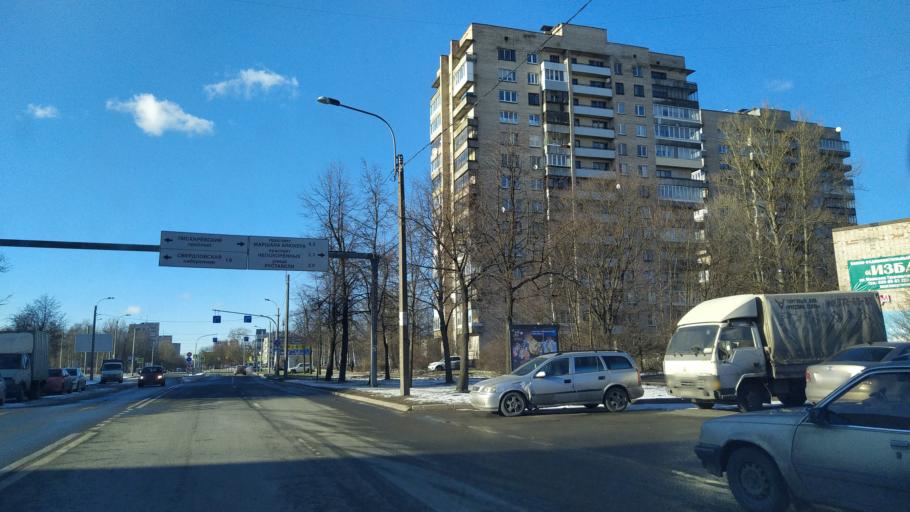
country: RU
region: Leningrad
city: Kalininskiy
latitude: 59.9728
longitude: 30.4169
